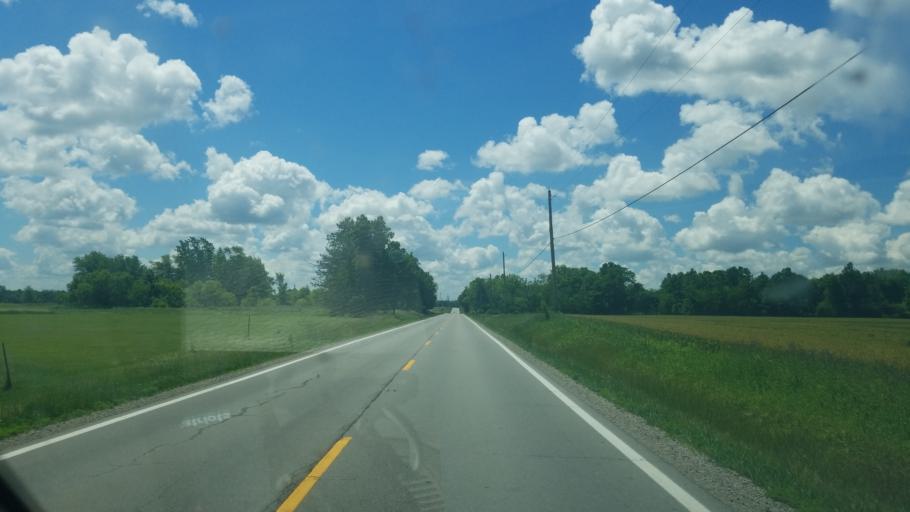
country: US
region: Ohio
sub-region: Huron County
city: New London
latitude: 41.1532
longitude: -82.4101
